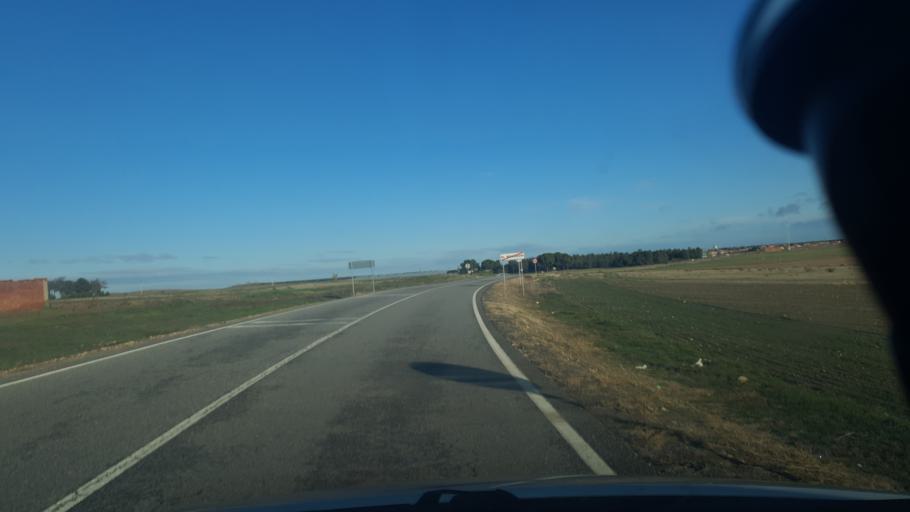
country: ES
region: Castille and Leon
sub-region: Provincia de Avila
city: Tinosillos
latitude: 40.9170
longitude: -4.7290
